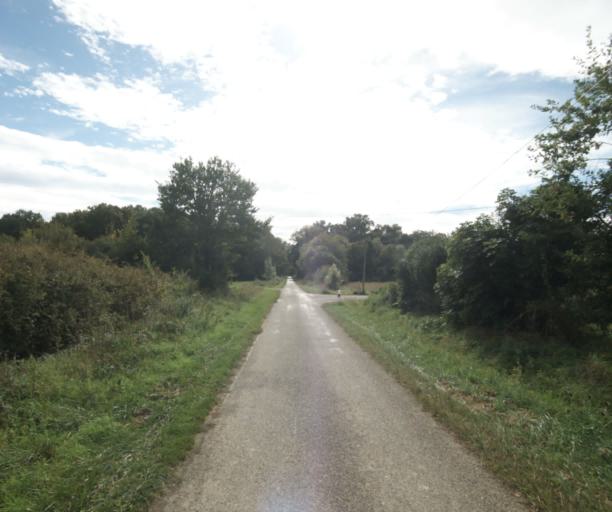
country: FR
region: Aquitaine
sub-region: Departement des Landes
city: Villeneuve-de-Marsan
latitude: 43.8885
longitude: -0.2001
